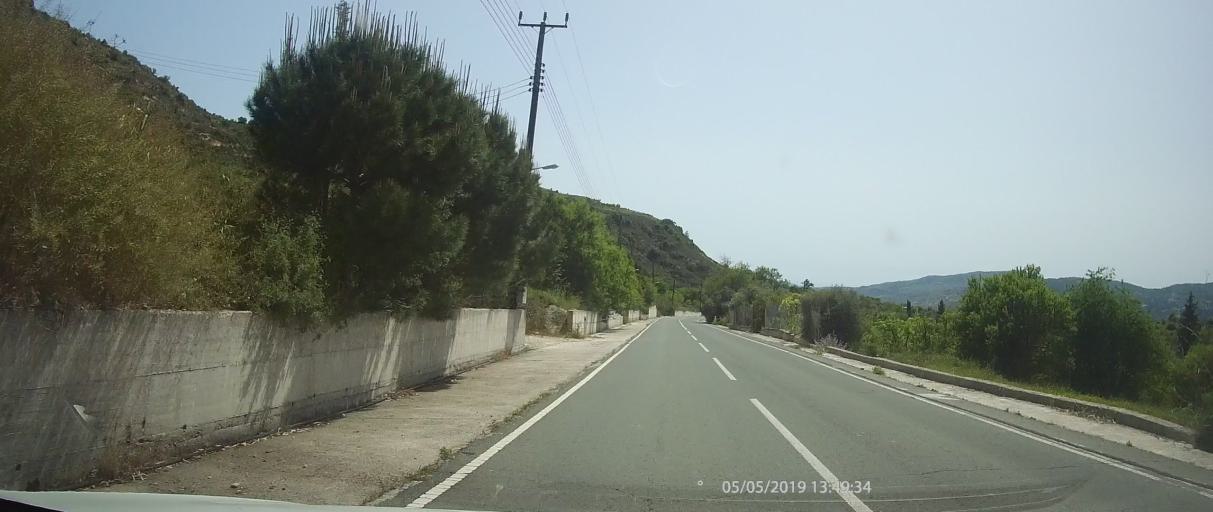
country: CY
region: Limassol
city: Pachna
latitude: 34.8482
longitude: 32.7480
